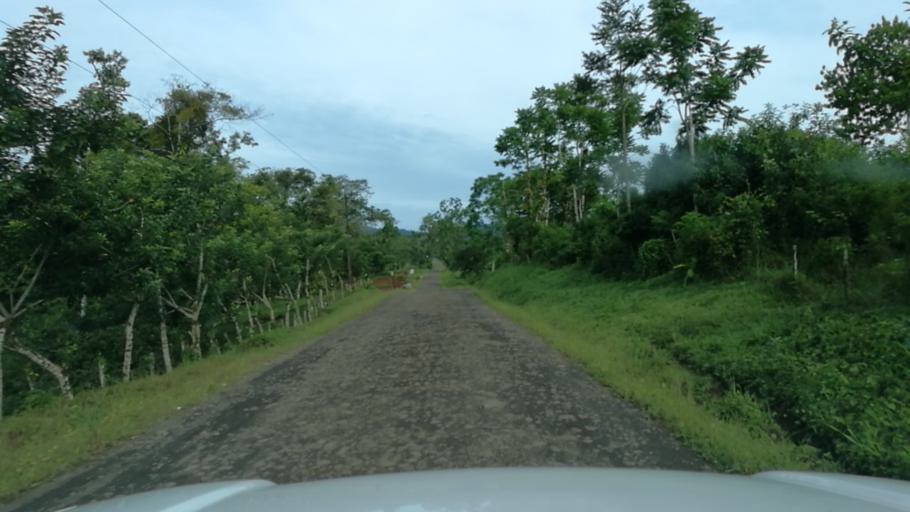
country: CR
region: Alajuela
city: Bijagua
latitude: 10.7127
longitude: -84.9172
